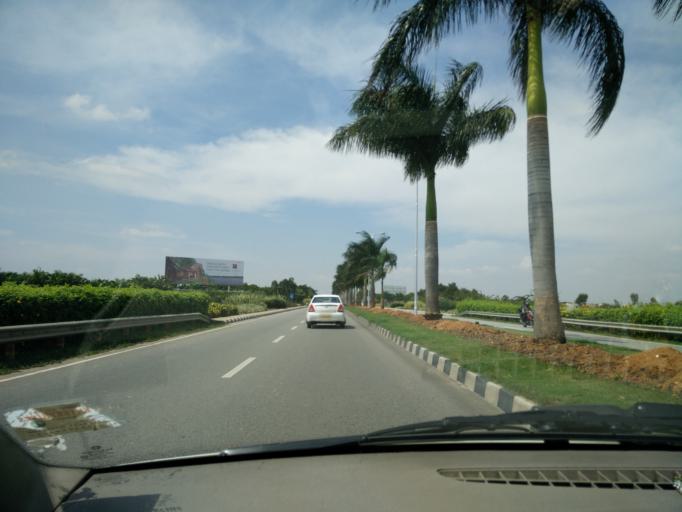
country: IN
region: Karnataka
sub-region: Bangalore Rural
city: Devanhalli
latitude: 13.1980
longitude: 77.6969
